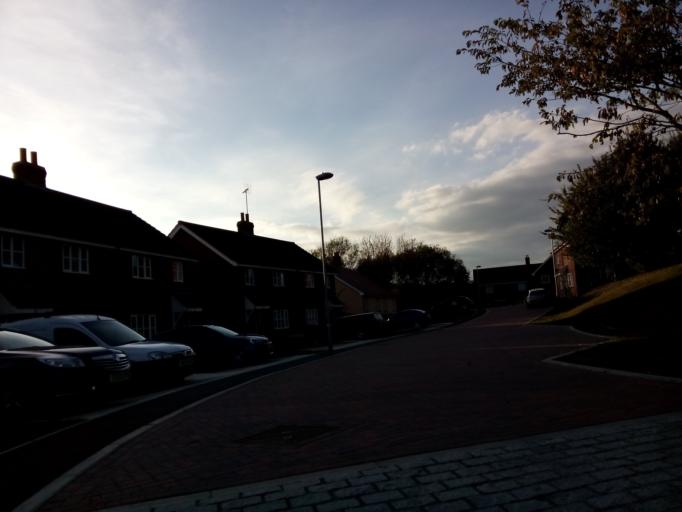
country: GB
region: England
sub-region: Suffolk
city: Bramford
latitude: 52.0387
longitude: 1.0916
